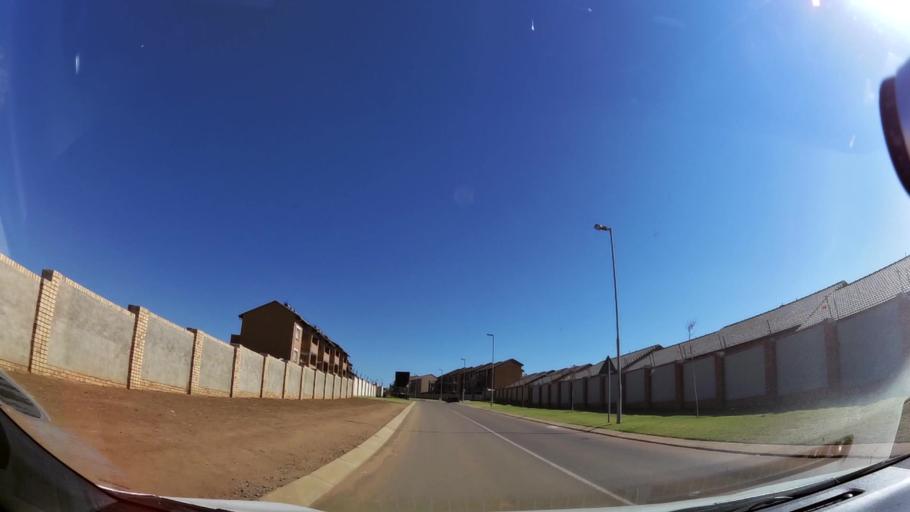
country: ZA
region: Gauteng
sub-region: City of Johannesburg Metropolitan Municipality
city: Midrand
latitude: -25.9482
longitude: 28.1061
